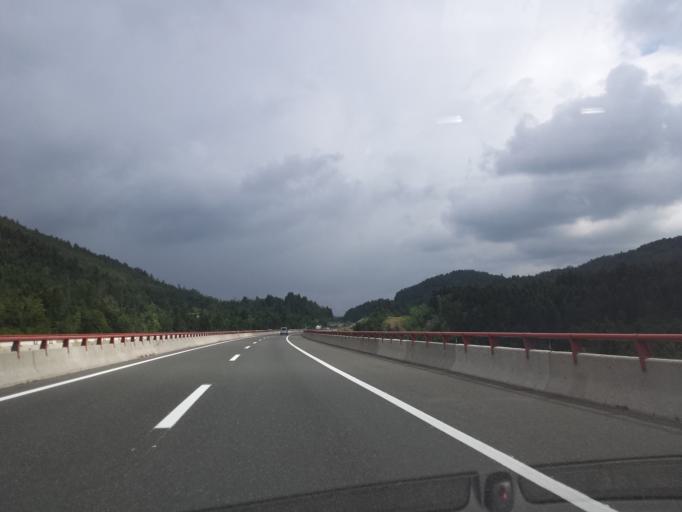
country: HR
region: Primorsko-Goranska
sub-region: Grad Delnice
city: Delnice
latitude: 45.3557
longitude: 14.7615
